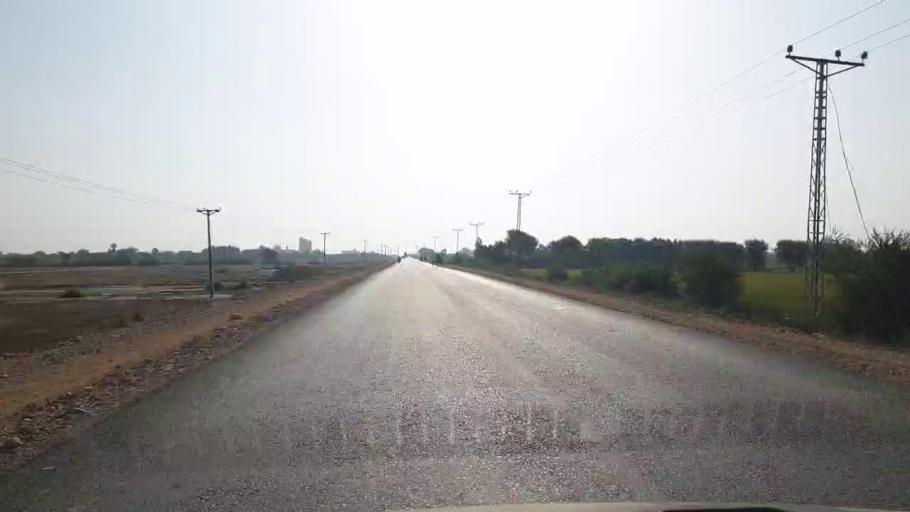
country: PK
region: Sindh
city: Badin
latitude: 24.6643
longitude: 68.8722
